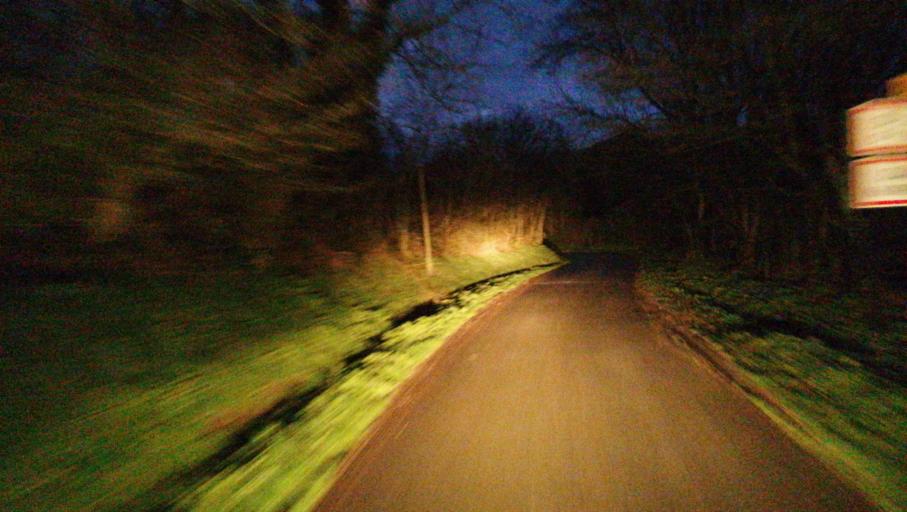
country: FR
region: Brittany
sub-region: Departement des Cotes-d'Armor
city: Plehedel
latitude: 48.6801
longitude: -3.0417
